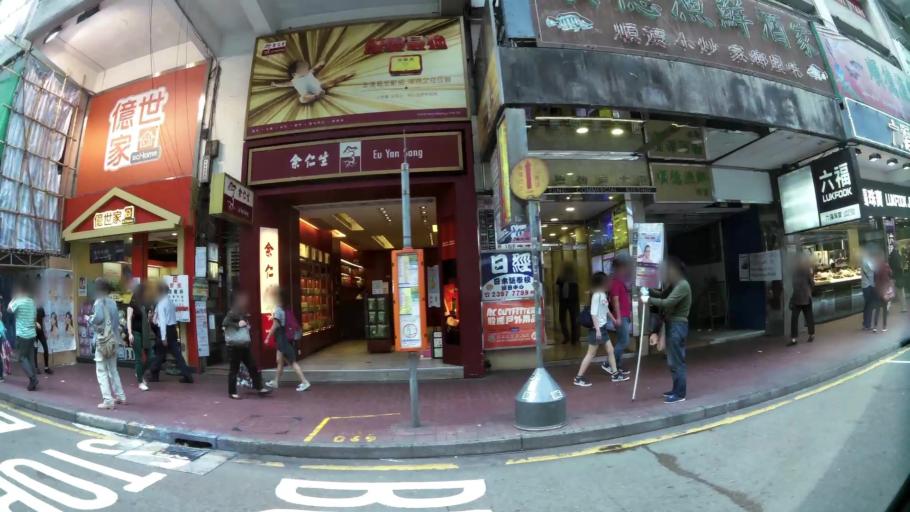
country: HK
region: Wanchai
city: Wan Chai
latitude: 22.2797
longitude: 114.1822
